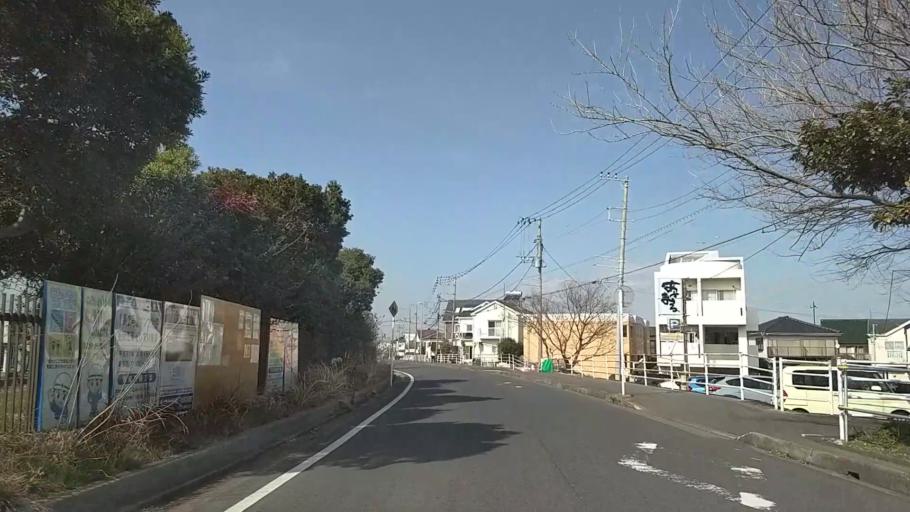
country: JP
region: Kanagawa
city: Chigasaki
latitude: 35.3196
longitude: 139.3815
